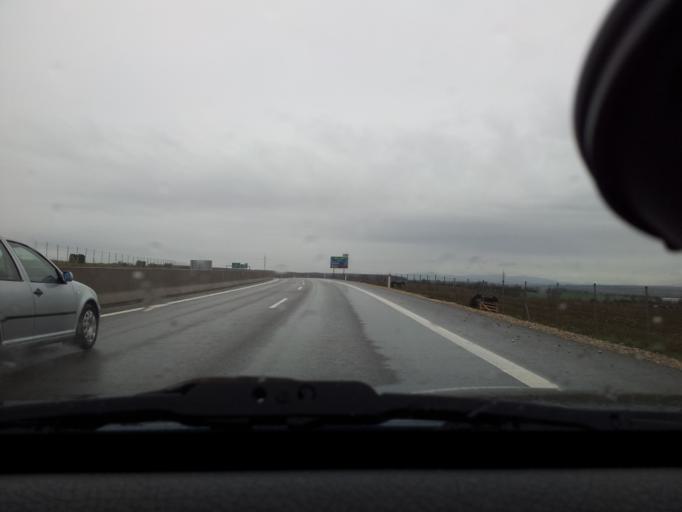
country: SK
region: Nitriansky
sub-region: Okres Nitra
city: Nitra
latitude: 48.3090
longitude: 18.0178
